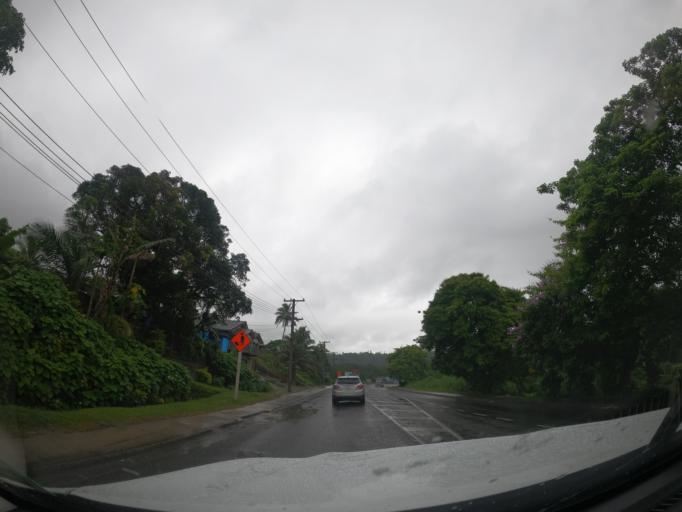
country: FJ
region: Central
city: Suva
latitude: -18.1132
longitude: 178.4283
